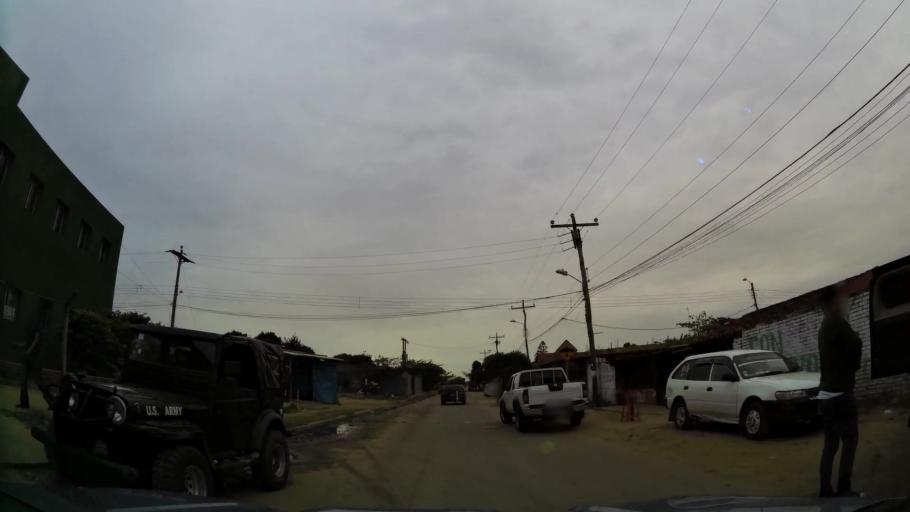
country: BO
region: Santa Cruz
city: Santa Cruz de la Sierra
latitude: -17.8614
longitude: -63.1719
